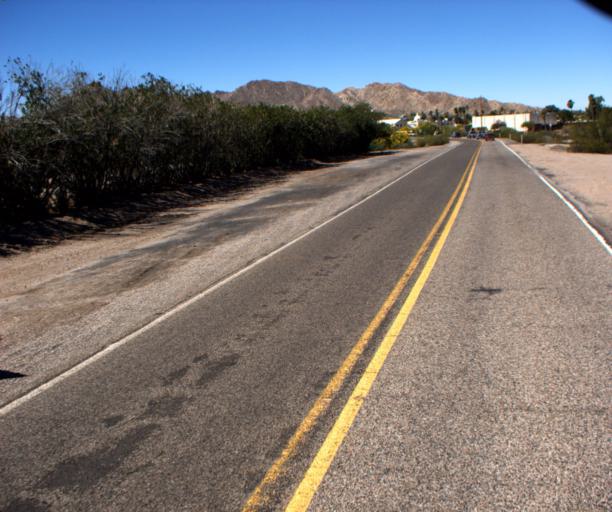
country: US
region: Arizona
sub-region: Pima County
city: Ajo
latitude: 32.3721
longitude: -112.8560
